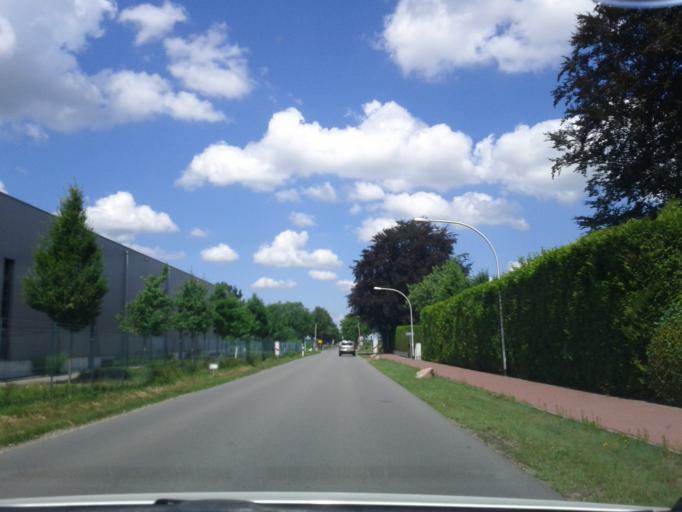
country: DE
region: Lower Saxony
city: Apensen
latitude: 53.4401
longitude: 9.6108
